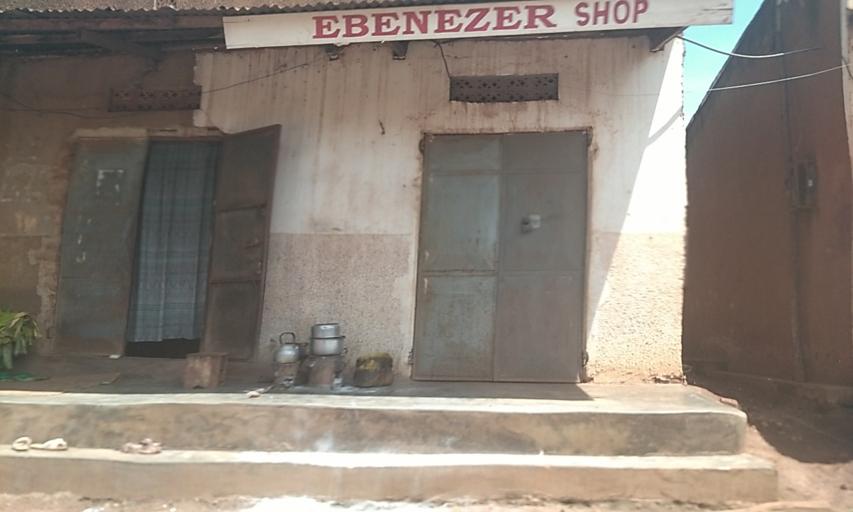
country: UG
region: Central Region
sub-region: Wakiso District
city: Wakiso
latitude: 0.4051
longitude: 32.4731
